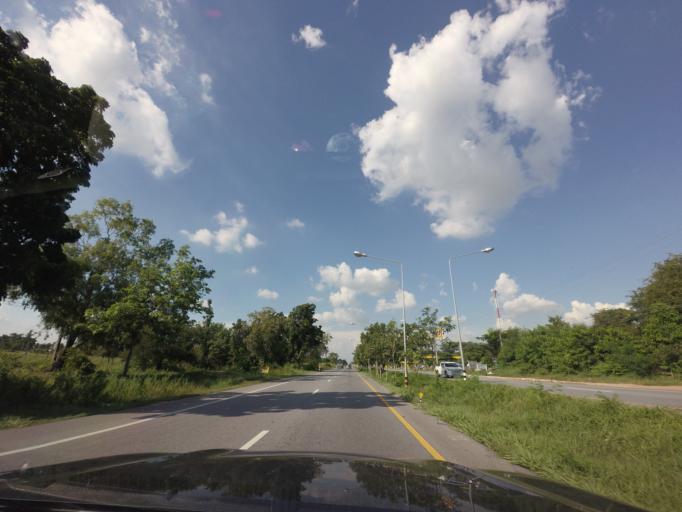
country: TH
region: Khon Kaen
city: Phon
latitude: 15.7298
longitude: 102.5950
